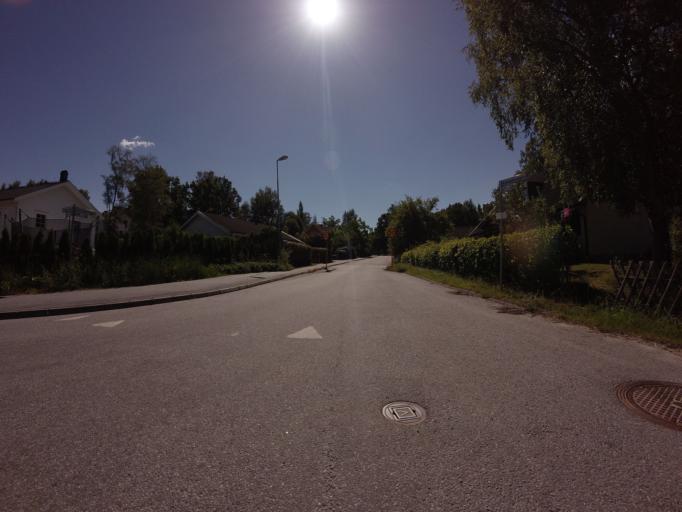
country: SE
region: Stockholm
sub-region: Sollentuna Kommun
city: Sollentuna
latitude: 59.4556
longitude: 17.8940
